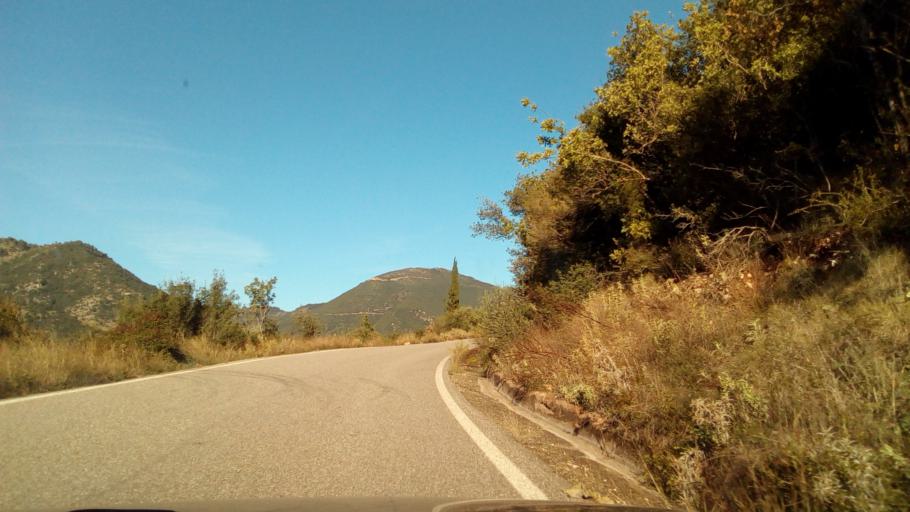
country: GR
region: West Greece
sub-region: Nomos Aitolias kai Akarnanias
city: Nafpaktos
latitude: 38.4742
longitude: 21.8726
